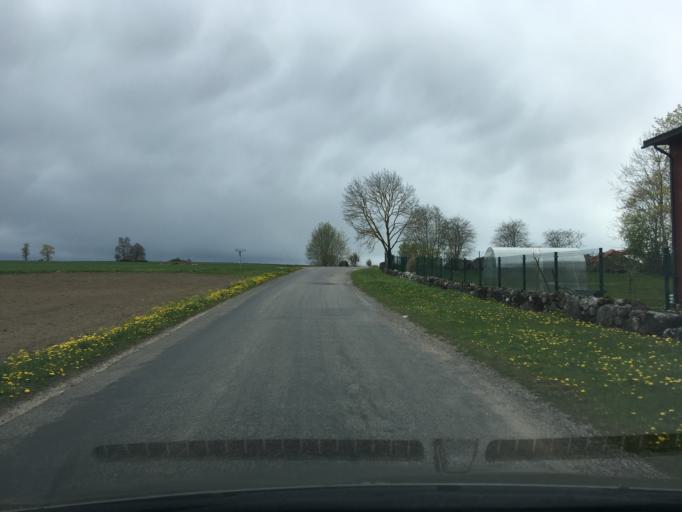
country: EE
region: Harju
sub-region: Rae vald
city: Vaida
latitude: 59.3630
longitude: 24.9702
